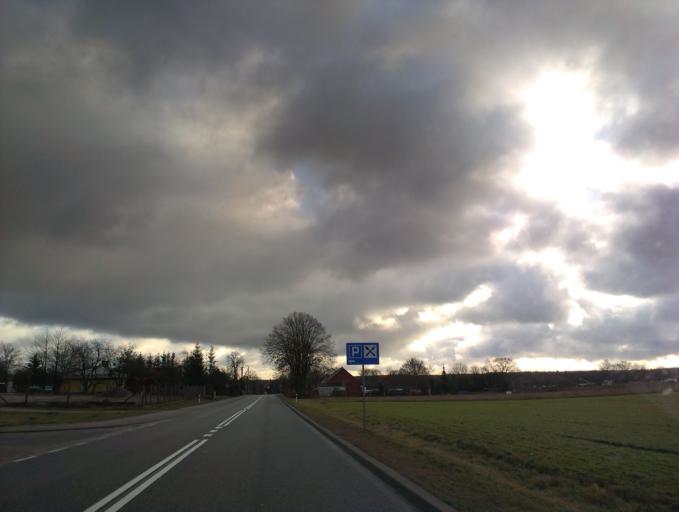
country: PL
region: Pomeranian Voivodeship
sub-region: Powiat czluchowski
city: Debrzno
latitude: 53.6259
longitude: 17.2244
